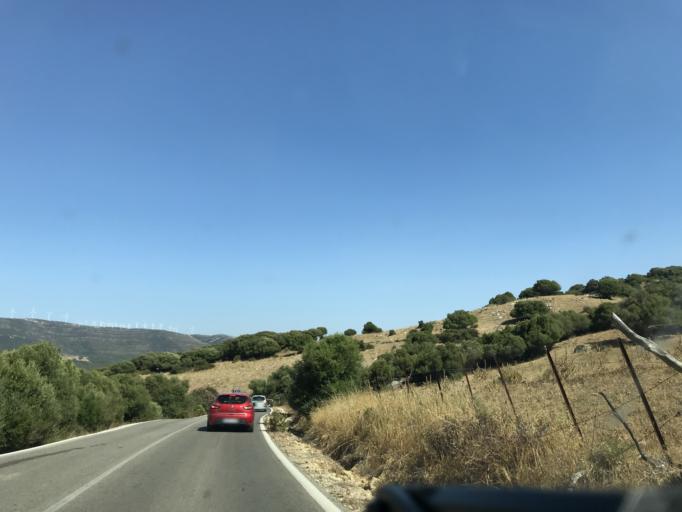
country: ES
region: Andalusia
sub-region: Provincia de Cadiz
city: Zahara de los Atunes
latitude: 36.1013
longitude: -5.7216
